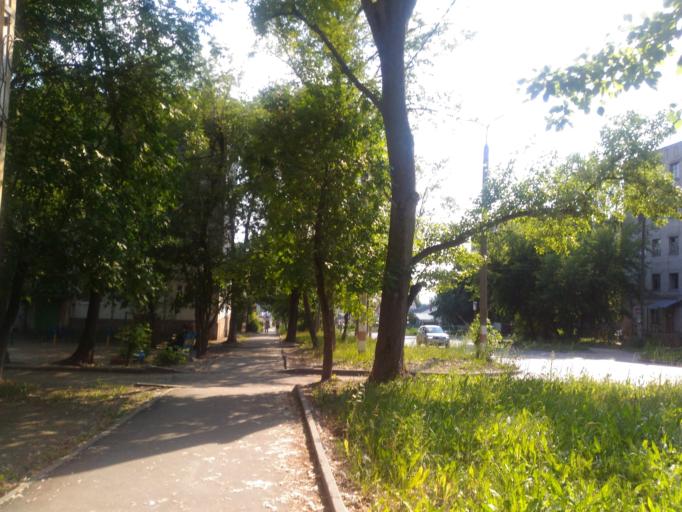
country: RU
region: Ulyanovsk
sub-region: Ulyanovskiy Rayon
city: Ulyanovsk
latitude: 54.3410
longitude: 48.3681
